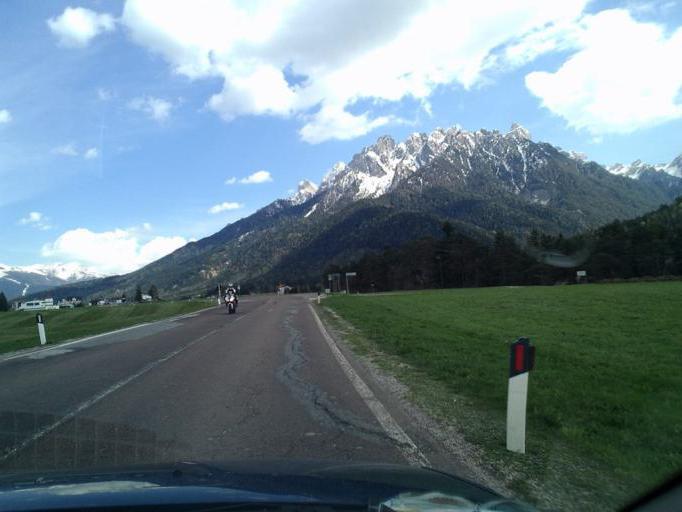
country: IT
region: Trentino-Alto Adige
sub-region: Bolzano
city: Dobbiaco
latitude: 46.7307
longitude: 12.2092
